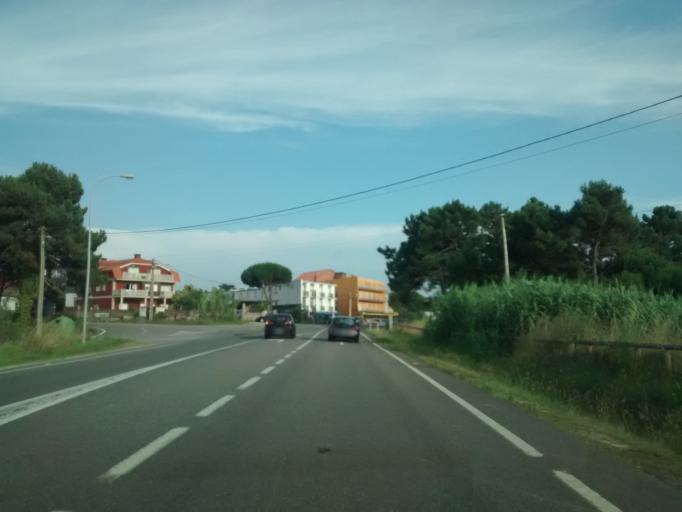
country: ES
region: Galicia
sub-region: Provincia de Pontevedra
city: Sanxenxo
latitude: 42.3990
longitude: -8.8460
